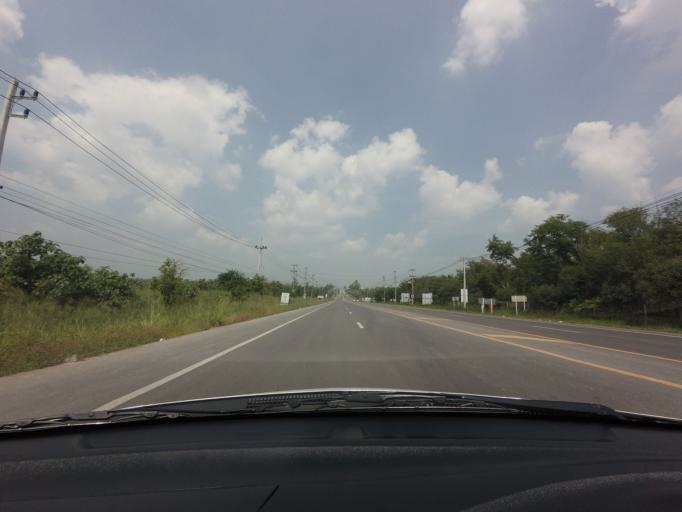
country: TH
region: Nakhon Ratchasima
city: Pak Chong
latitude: 14.6663
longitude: 101.4583
